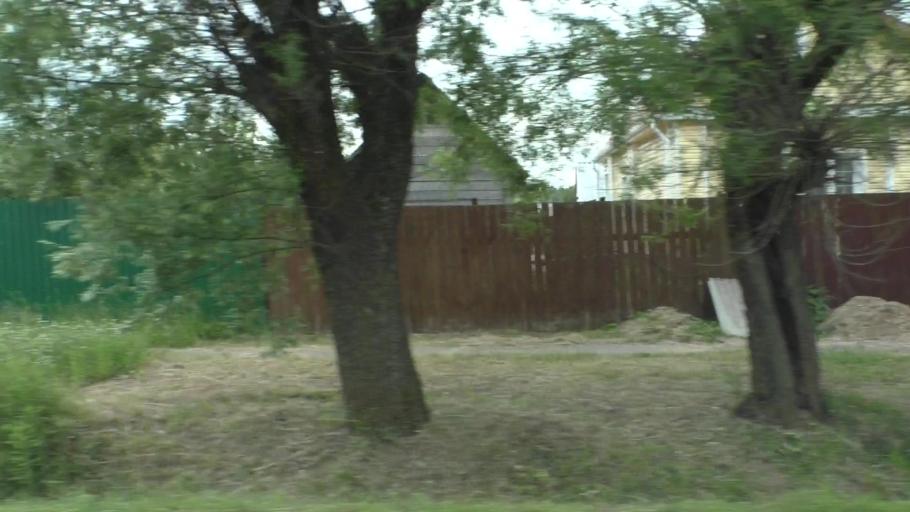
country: RU
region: Moskovskaya
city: Il'inskiy Pogost
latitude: 55.5025
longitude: 38.7939
